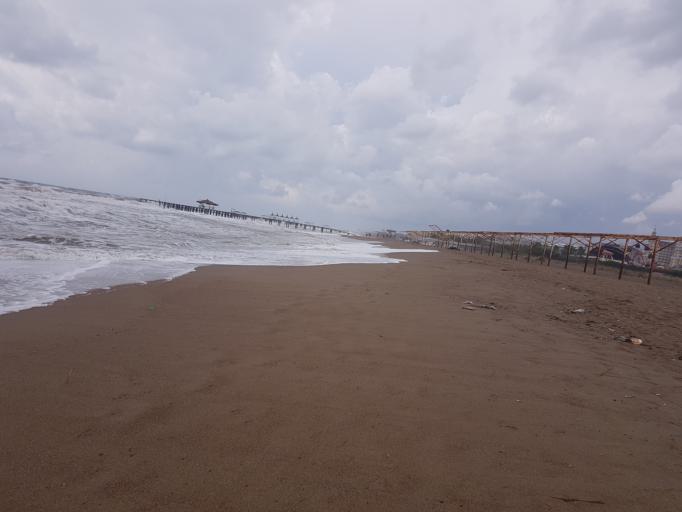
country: TR
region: Antalya
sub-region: Serik
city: Kumkoey
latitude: 36.8536
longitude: 30.8985
